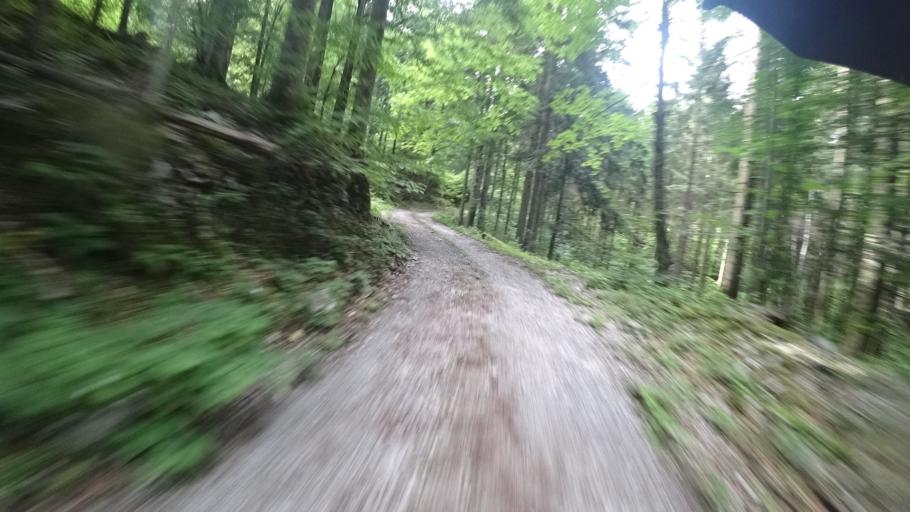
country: SI
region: Osilnica
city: Osilnica
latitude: 45.4831
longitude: 14.6812
